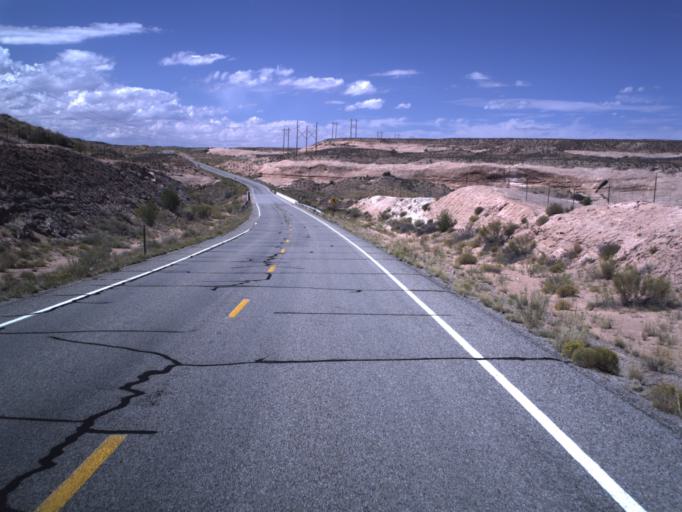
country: US
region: Utah
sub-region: San Juan County
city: Blanding
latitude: 37.3007
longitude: -109.4541
